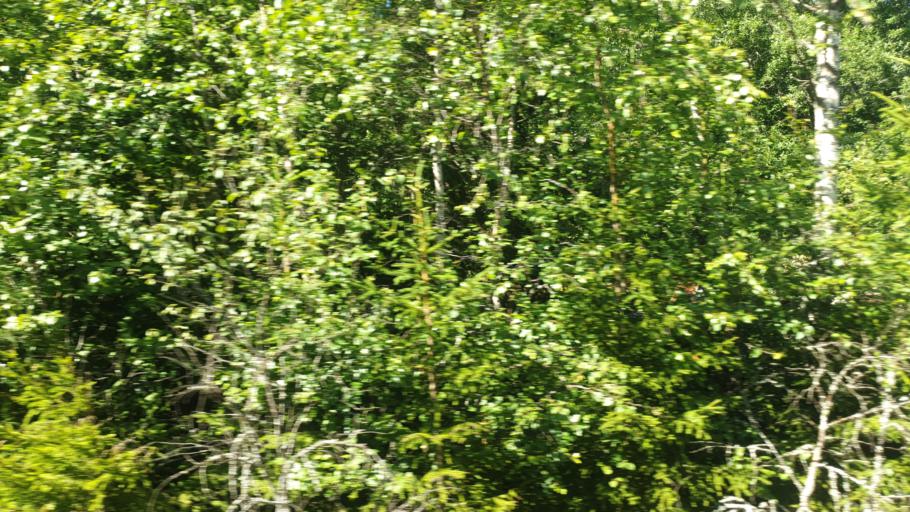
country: NO
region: Sor-Trondelag
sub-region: Meldal
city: Meldal
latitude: 63.1314
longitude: 9.7083
